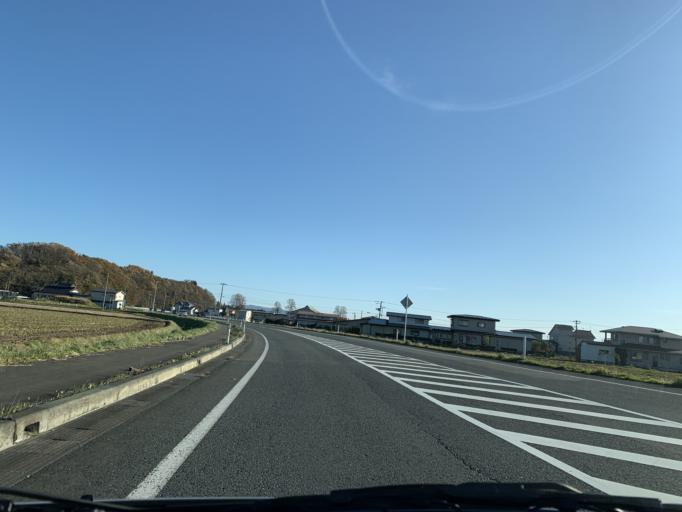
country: JP
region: Iwate
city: Kitakami
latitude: 39.2409
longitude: 141.1183
